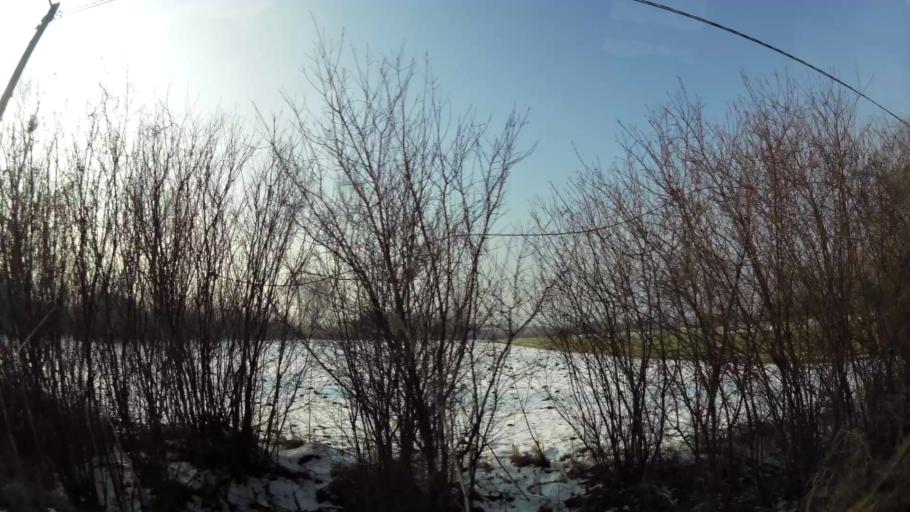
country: MK
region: Petrovec
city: Petrovec
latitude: 41.9467
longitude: 21.5957
